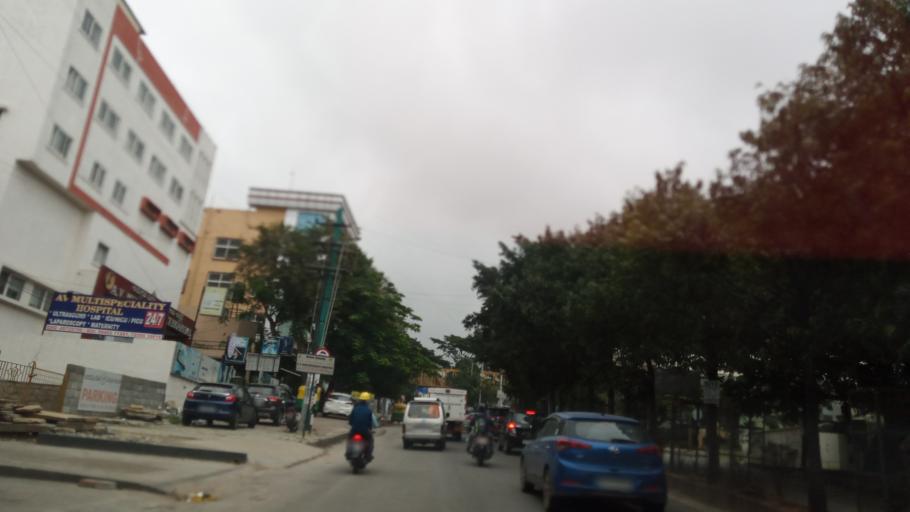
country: IN
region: Karnataka
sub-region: Bangalore Urban
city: Bangalore
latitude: 12.9328
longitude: 77.5407
